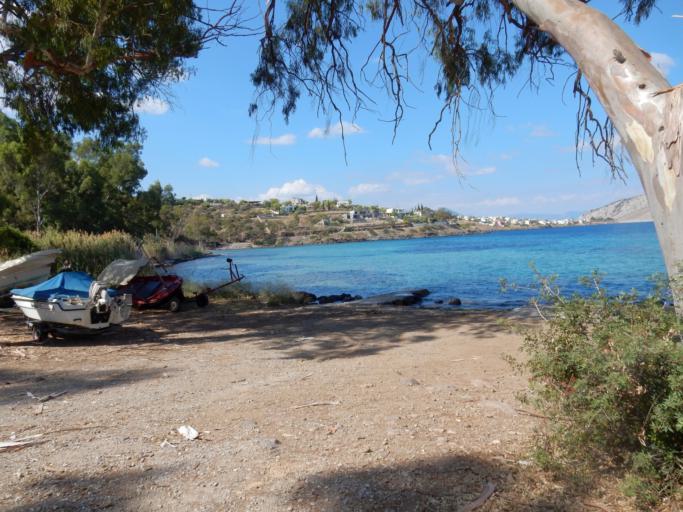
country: GR
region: Attica
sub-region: Nomos Piraios
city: Kypseli
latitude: 37.6999
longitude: 23.4689
